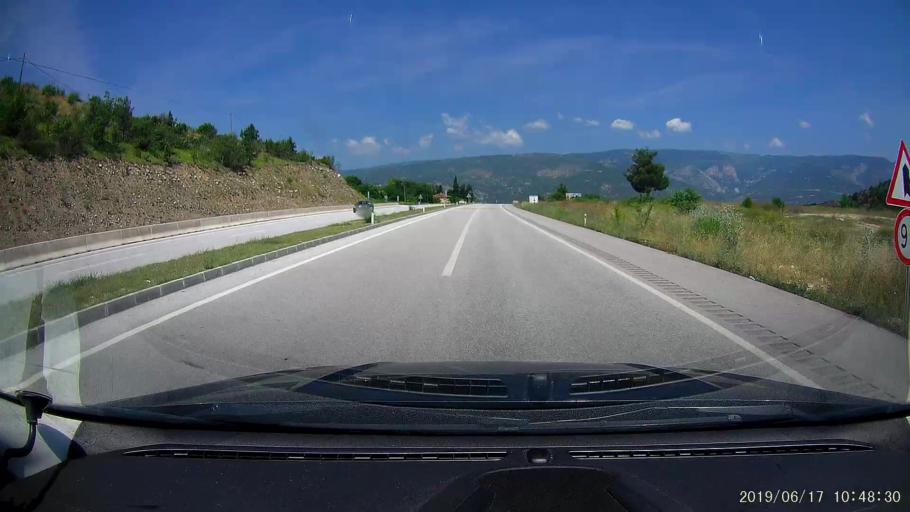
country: TR
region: Corum
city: Hacihamza
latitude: 41.0897
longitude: 34.4277
